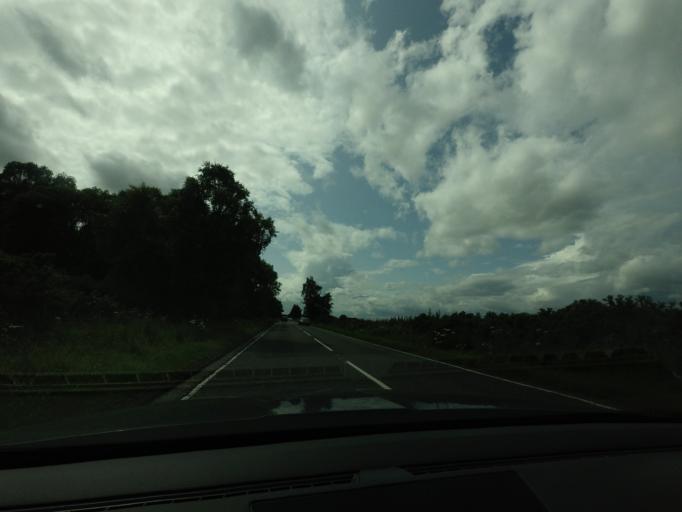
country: GB
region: Scotland
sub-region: Highland
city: Nairn
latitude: 57.5839
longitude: -3.7563
